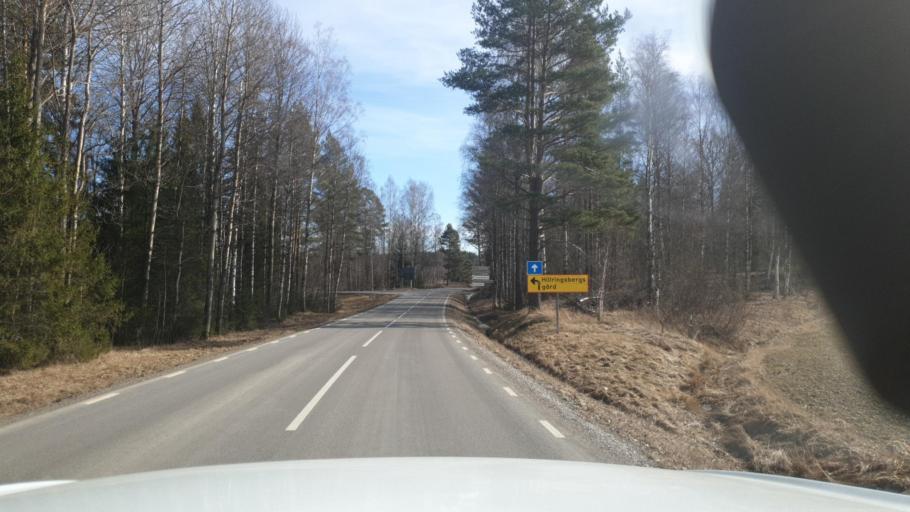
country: SE
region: Vaermland
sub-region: Arvika Kommun
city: Arvika
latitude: 59.5305
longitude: 12.6118
